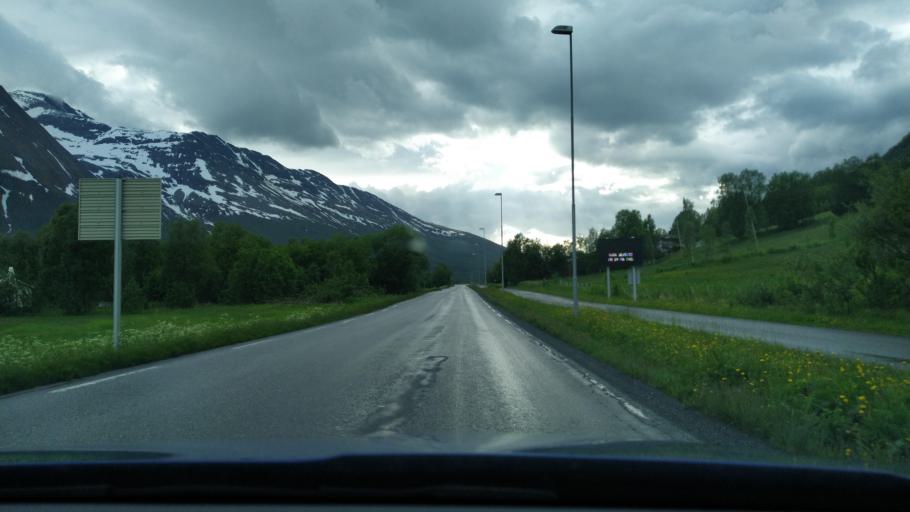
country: NO
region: Troms
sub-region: Balsfjord
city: Storsteinnes
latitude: 69.2201
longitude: 19.5486
